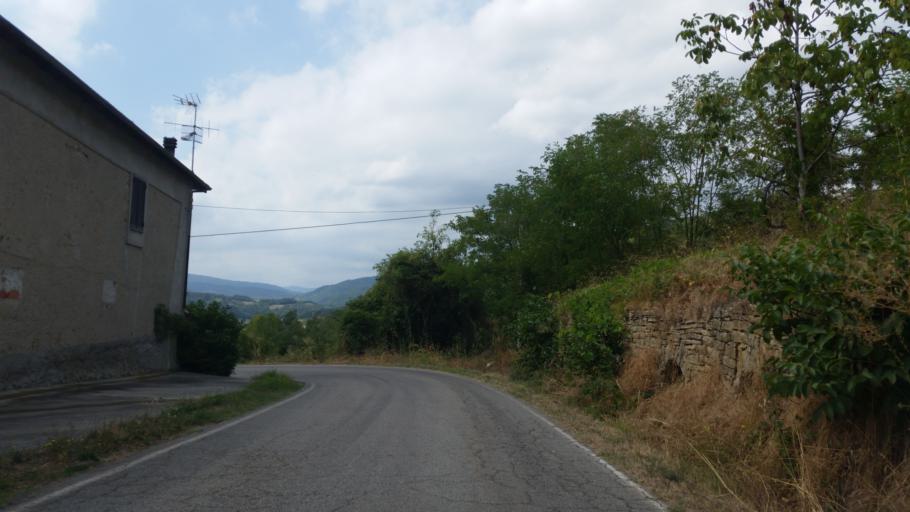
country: IT
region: Piedmont
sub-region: Provincia di Asti
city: Vesime
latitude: 44.6406
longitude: 8.2300
